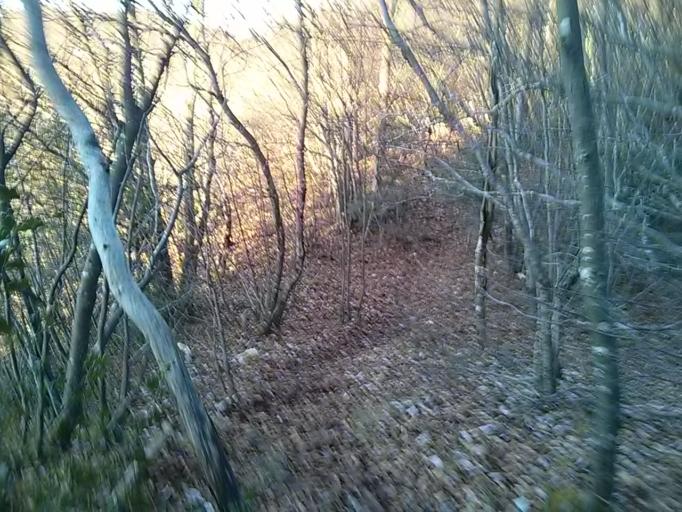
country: FR
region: Rhone-Alpes
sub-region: Departement de la Savoie
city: Chindrieux
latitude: 45.8023
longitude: 5.8727
